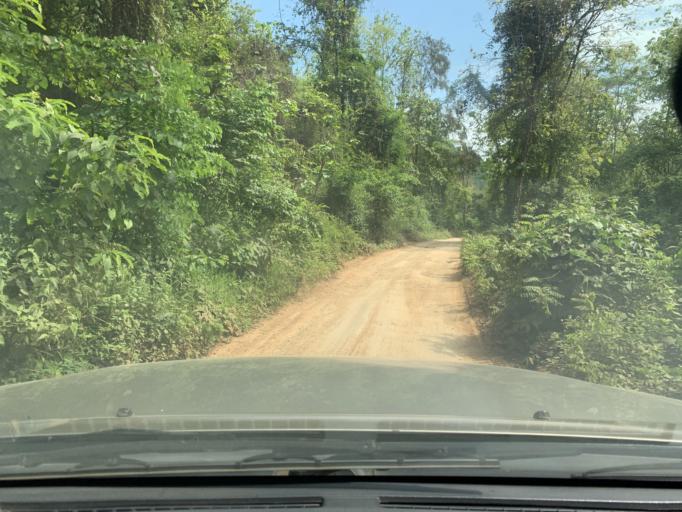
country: LA
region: Louangphabang
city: Louangphabang
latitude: 19.8884
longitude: 102.1981
